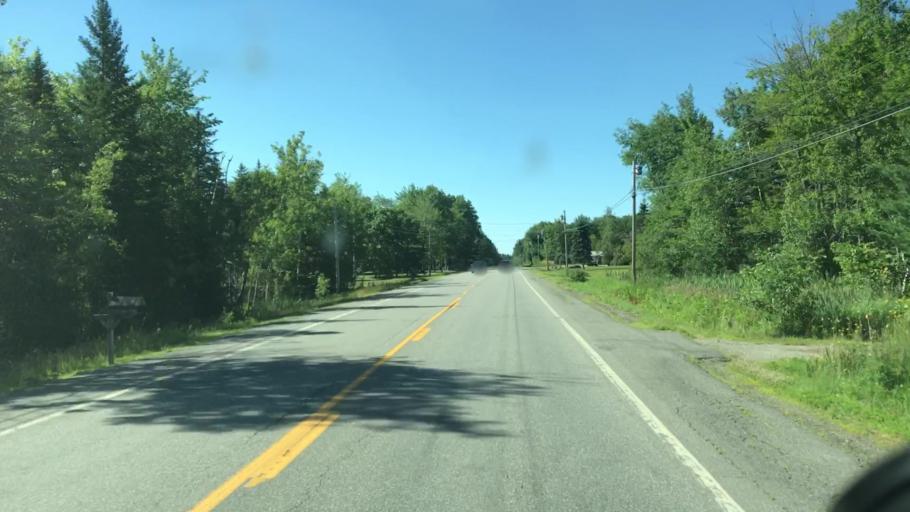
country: US
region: Maine
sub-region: Penobscot County
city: Howland
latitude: 45.2674
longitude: -68.6387
